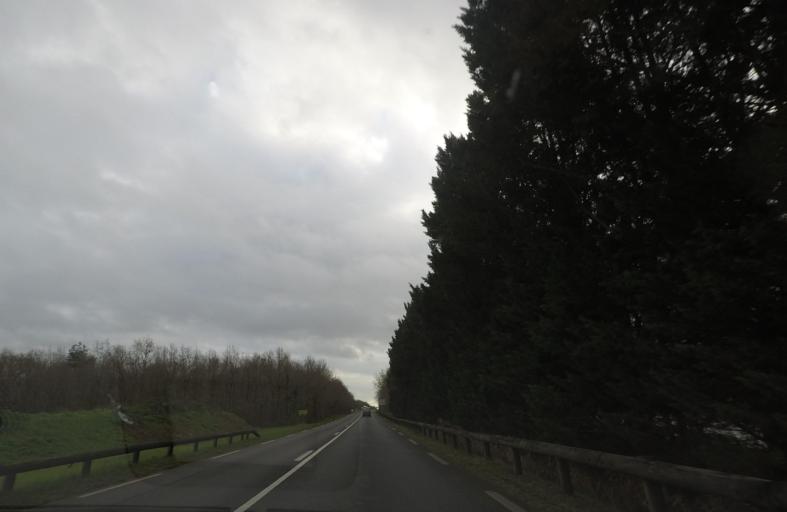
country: FR
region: Centre
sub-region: Departement du Loir-et-Cher
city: Soings-en-Sologne
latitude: 47.4581
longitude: 1.5245
